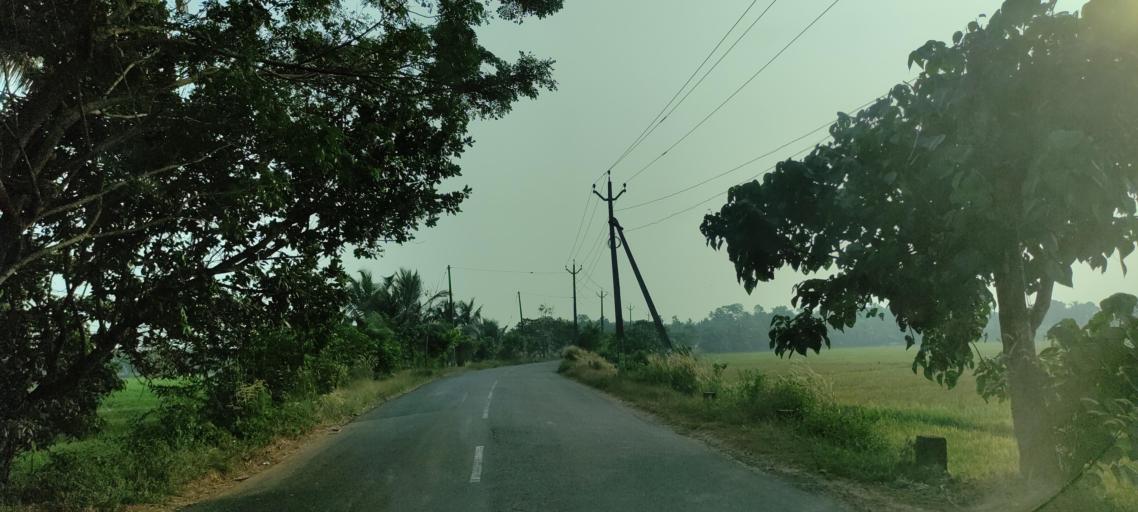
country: IN
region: Kerala
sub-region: Kottayam
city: Vaikam
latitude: 9.6866
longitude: 76.4635
